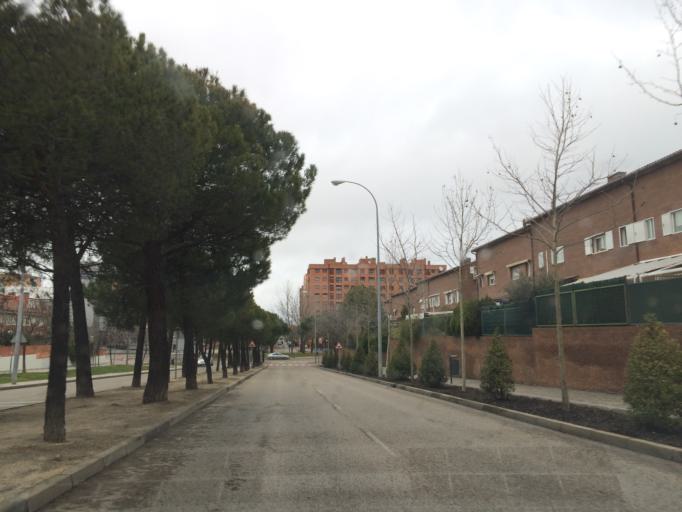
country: ES
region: Madrid
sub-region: Provincia de Madrid
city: Tres Cantos
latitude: 40.5979
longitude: -3.7071
